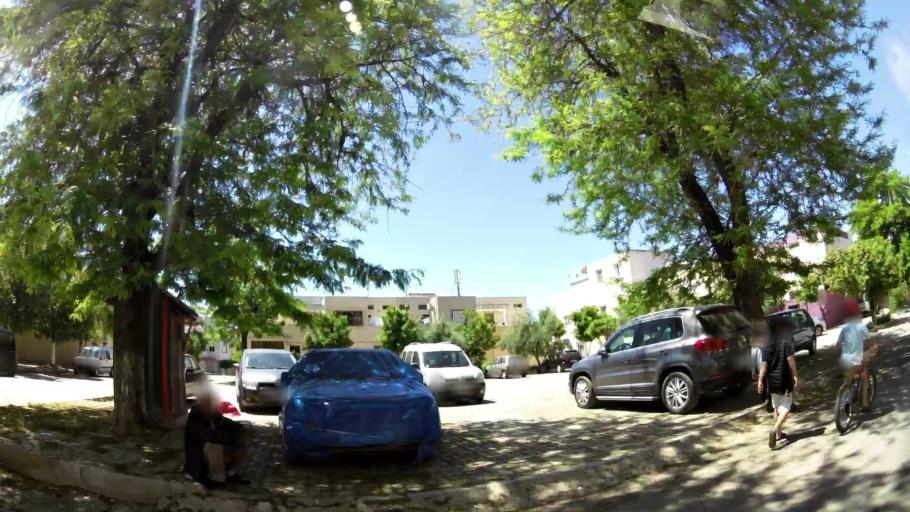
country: MA
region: Fes-Boulemane
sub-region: Fes
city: Fes
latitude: 34.0223
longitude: -5.0042
